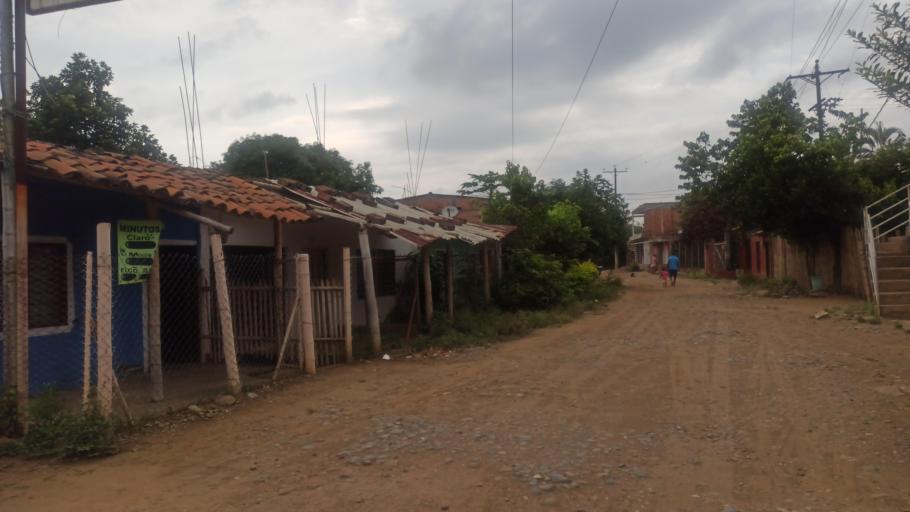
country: CO
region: Valle del Cauca
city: Jamundi
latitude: 3.1994
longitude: -76.5061
